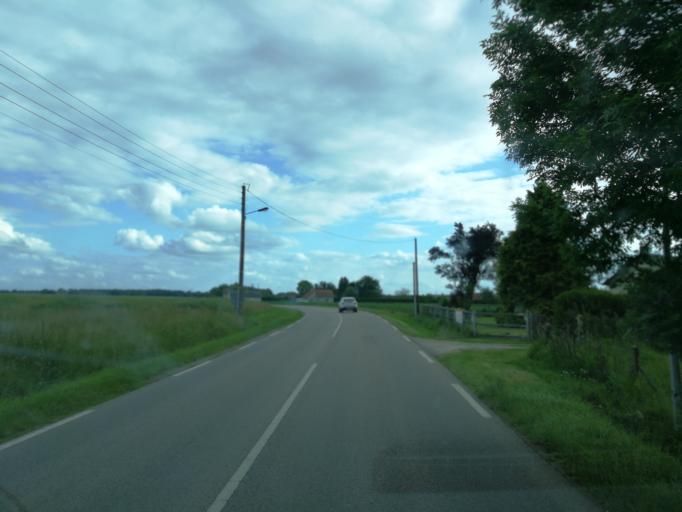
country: FR
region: Haute-Normandie
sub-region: Departement de l'Eure
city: Le Neubourg
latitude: 49.1781
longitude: 0.8776
